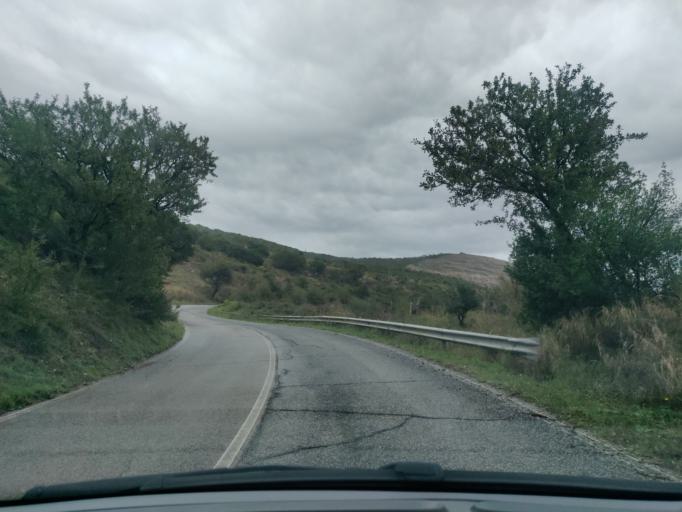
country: IT
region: Latium
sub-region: Citta metropolitana di Roma Capitale
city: Aurelia
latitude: 42.1307
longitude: 11.8443
